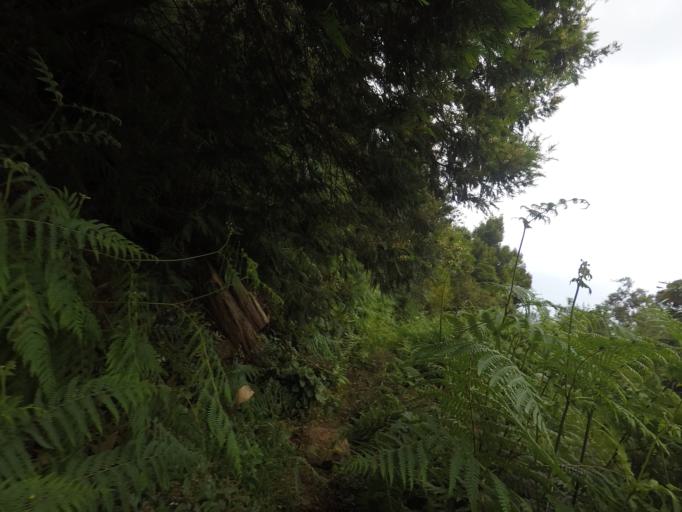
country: PT
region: Madeira
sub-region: Santa Cruz
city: Santa Cruz
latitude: 32.7500
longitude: -16.8251
